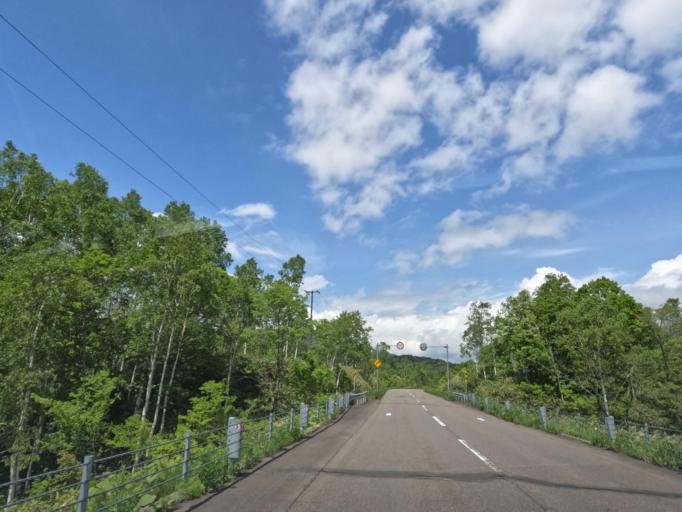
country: JP
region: Hokkaido
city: Tobetsu
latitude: 43.5259
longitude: 141.5884
